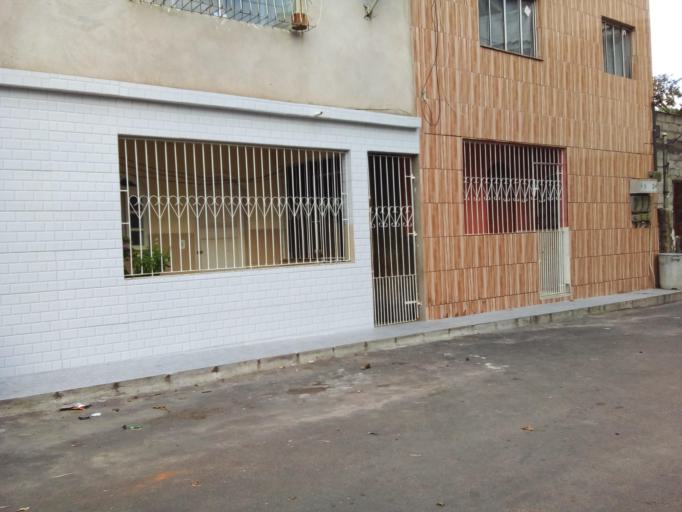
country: BR
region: Espirito Santo
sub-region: Serra
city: Serra
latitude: -20.2257
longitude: -40.2725
